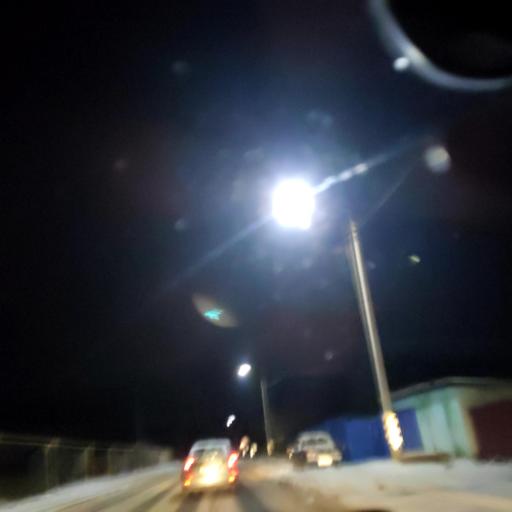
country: RU
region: Voronezj
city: Latnaya
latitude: 51.6629
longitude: 38.8898
